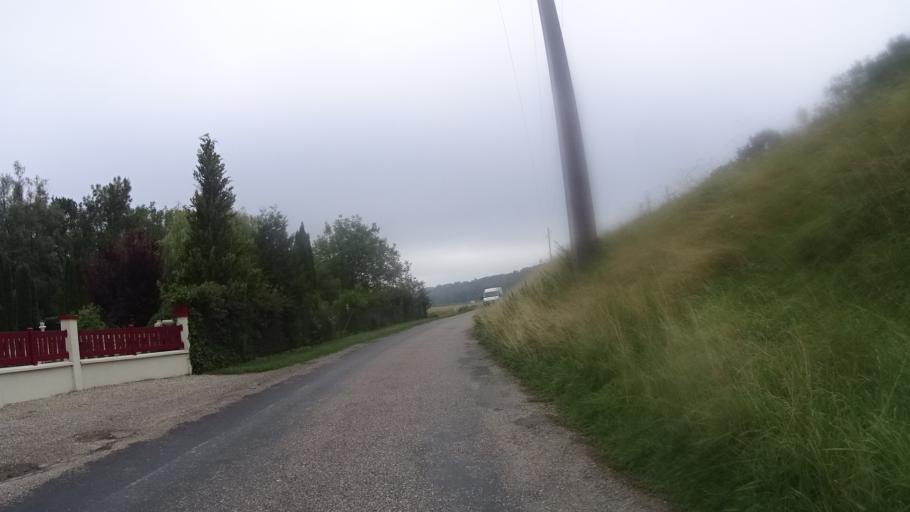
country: FR
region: Lorraine
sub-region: Departement de la Meuse
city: Revigny-sur-Ornain
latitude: 48.8151
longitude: 5.0441
